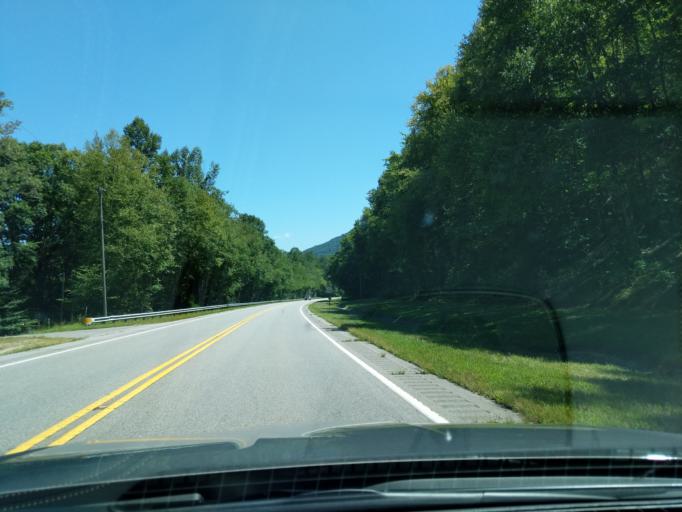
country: US
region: North Carolina
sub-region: Macon County
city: Franklin
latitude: 35.1380
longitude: -83.5010
